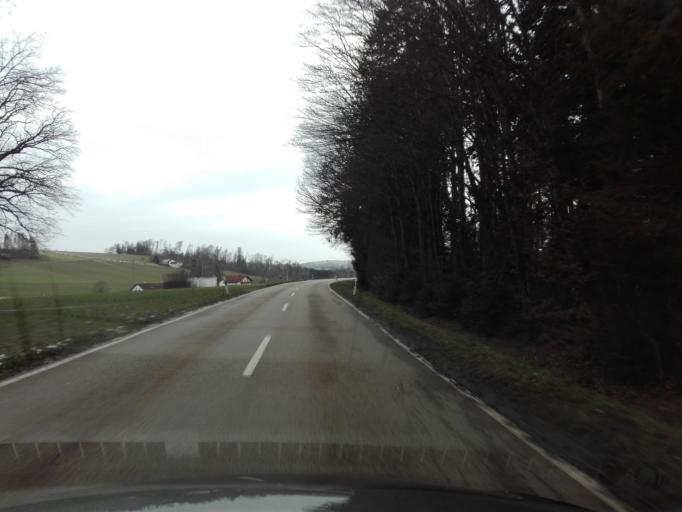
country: DE
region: Bavaria
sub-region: Lower Bavaria
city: Obernzell
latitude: 48.5906
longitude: 13.6282
